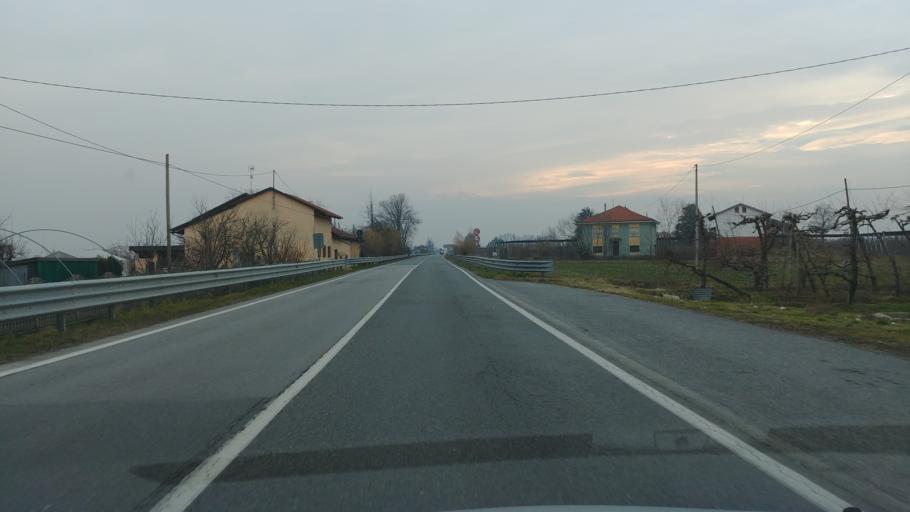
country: IT
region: Piedmont
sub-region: Provincia di Cuneo
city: Sant'Albano Stura
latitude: 44.5081
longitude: 7.6843
